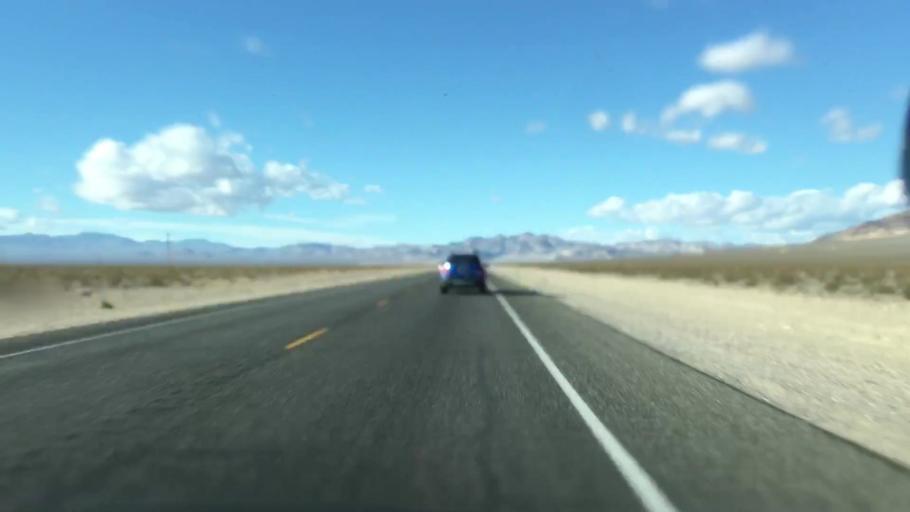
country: US
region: Nevada
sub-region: Nye County
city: Beatty
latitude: 36.7898
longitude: -116.7043
